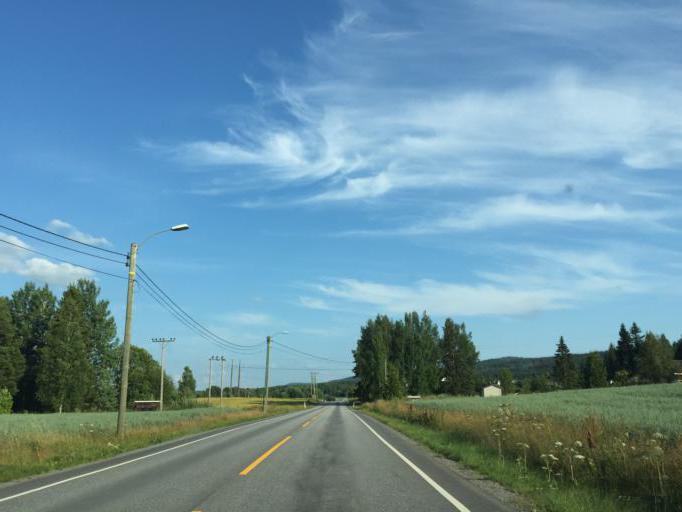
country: NO
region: Hedmark
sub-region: Sor-Odal
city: Skarnes
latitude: 60.2461
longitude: 11.7061
